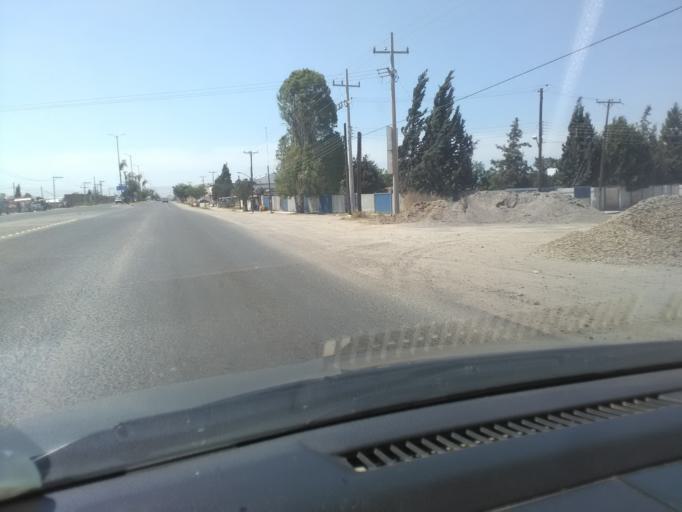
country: MX
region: Durango
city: Victoria de Durango
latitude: 24.0272
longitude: -104.5818
